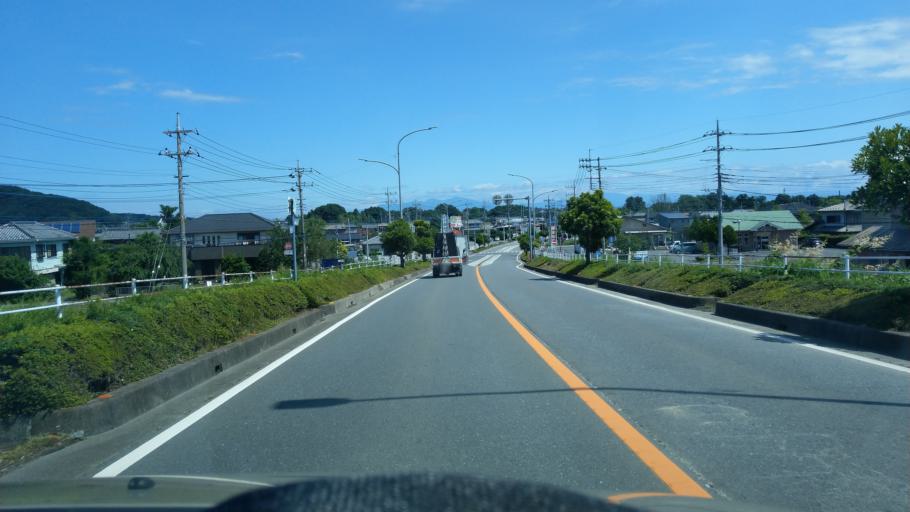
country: JP
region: Saitama
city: Yorii
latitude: 36.1151
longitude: 139.2106
